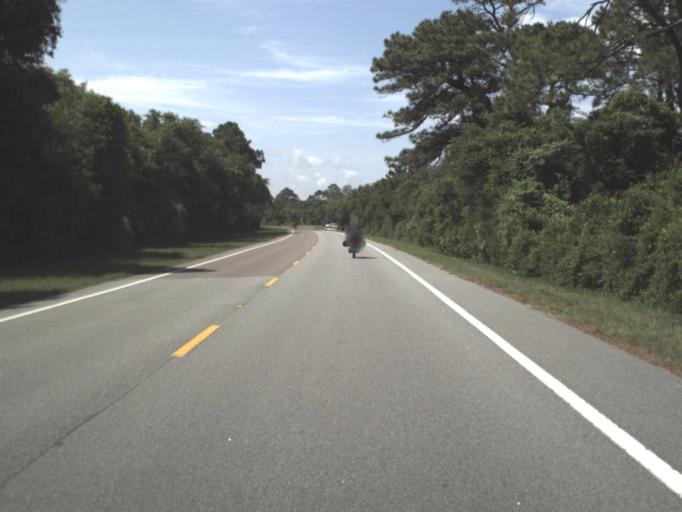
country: US
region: Florida
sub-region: Duval County
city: Atlantic Beach
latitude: 30.4885
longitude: -81.4408
